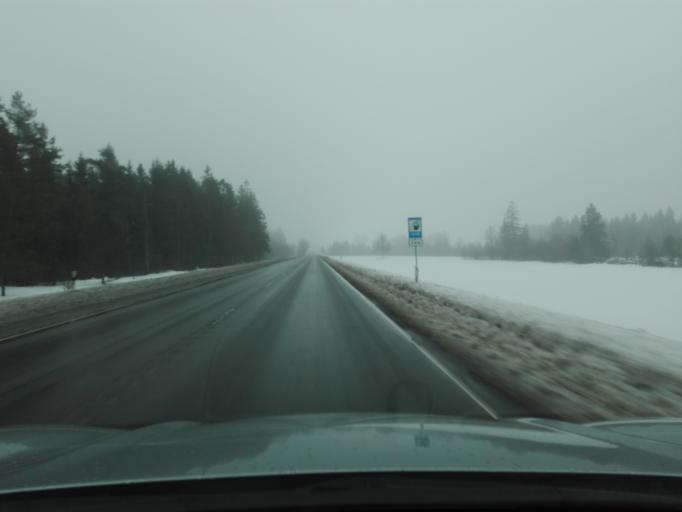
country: EE
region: Raplamaa
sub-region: Kohila vald
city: Kohila
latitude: 59.2068
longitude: 24.7803
